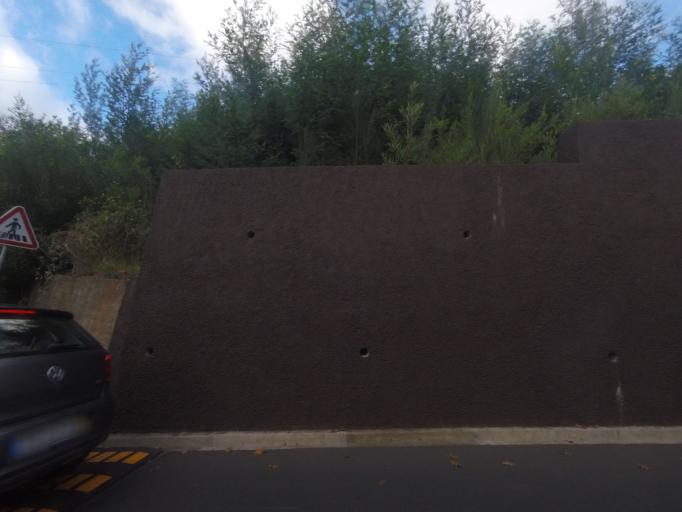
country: PT
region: Madeira
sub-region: Santa Cruz
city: Camacha
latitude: 32.6630
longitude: -16.8683
